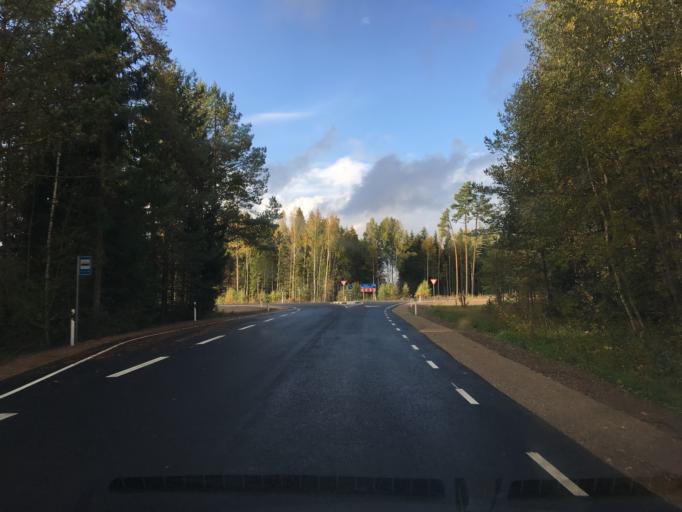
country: EE
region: Harju
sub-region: Nissi vald
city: Turba
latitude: 59.0880
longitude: 23.9810
